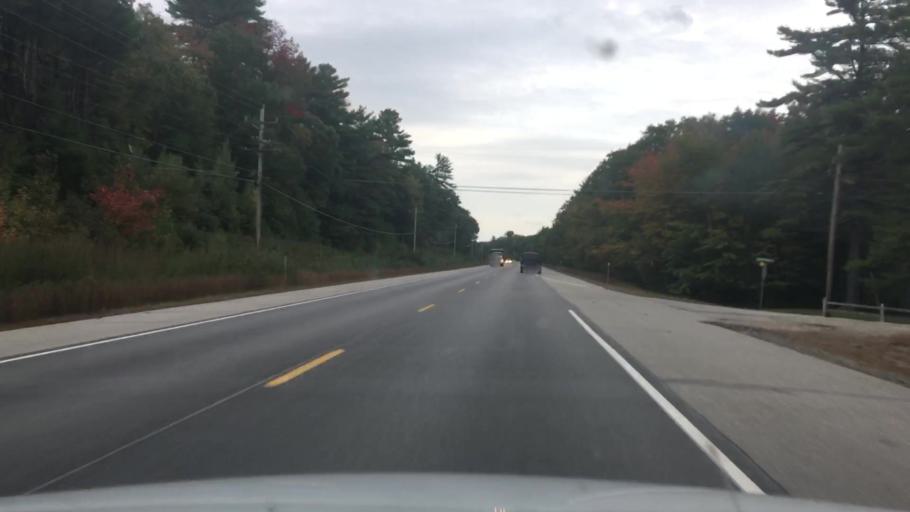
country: US
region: New Hampshire
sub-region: Strafford County
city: New Durham
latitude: 43.4393
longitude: -71.1924
